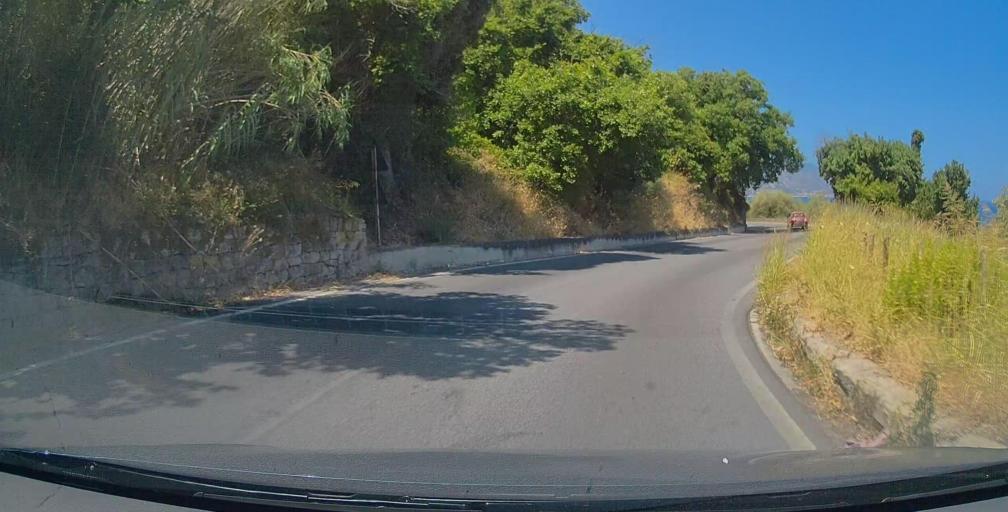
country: IT
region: Sicily
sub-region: Messina
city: Oliveri
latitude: 38.1417
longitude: 15.0140
